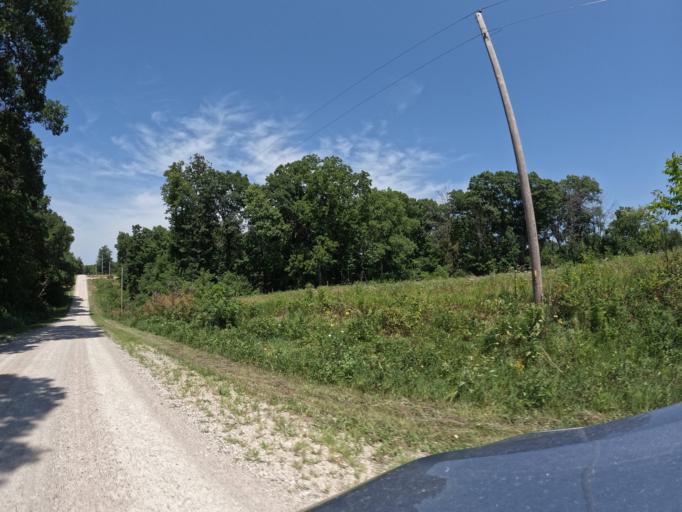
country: US
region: Iowa
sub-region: Henry County
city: Mount Pleasant
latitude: 40.9926
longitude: -91.6362
